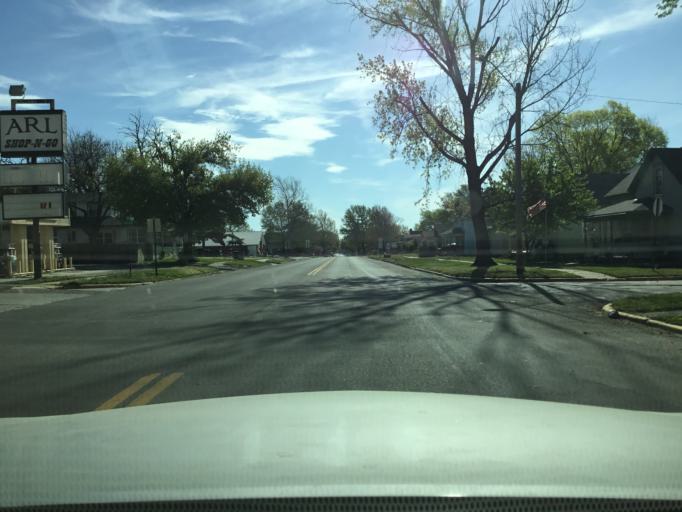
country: US
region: Kansas
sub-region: Neosho County
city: Chanute
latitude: 37.6820
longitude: -95.4665
